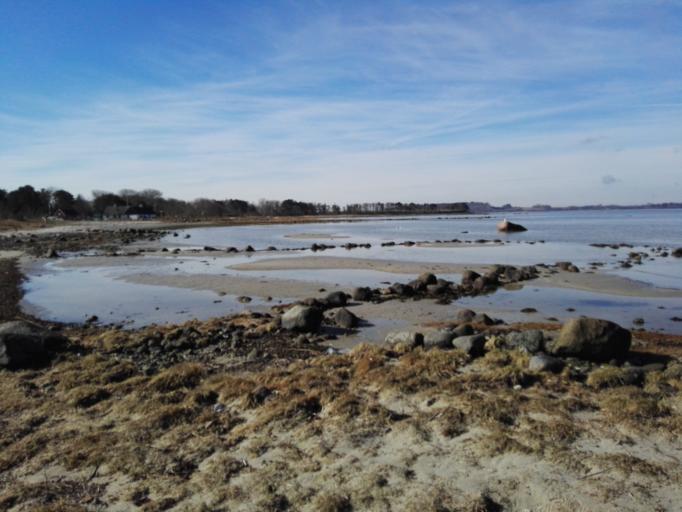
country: DK
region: Zealand
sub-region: Holbaek Kommune
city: Holbaek
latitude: 55.7889
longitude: 11.7958
